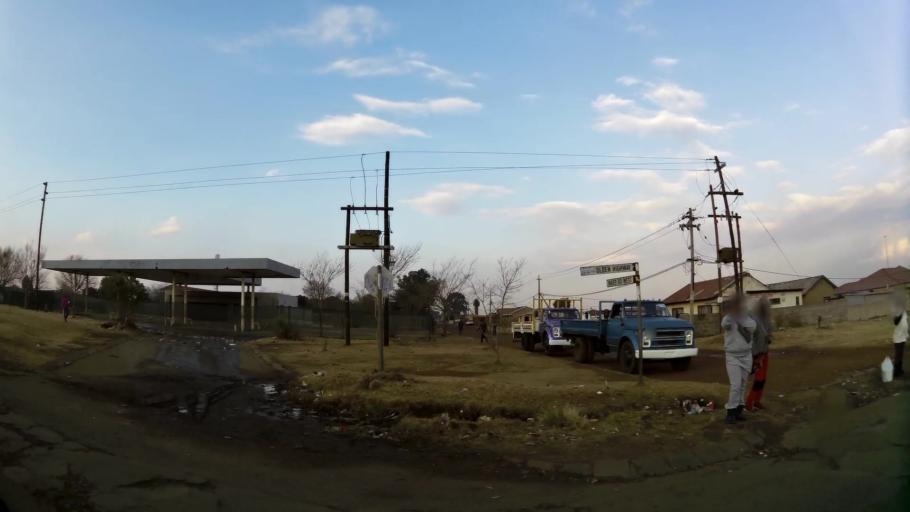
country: ZA
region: Gauteng
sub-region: City of Johannesburg Metropolitan Municipality
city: Orange Farm
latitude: -26.5392
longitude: 27.8324
